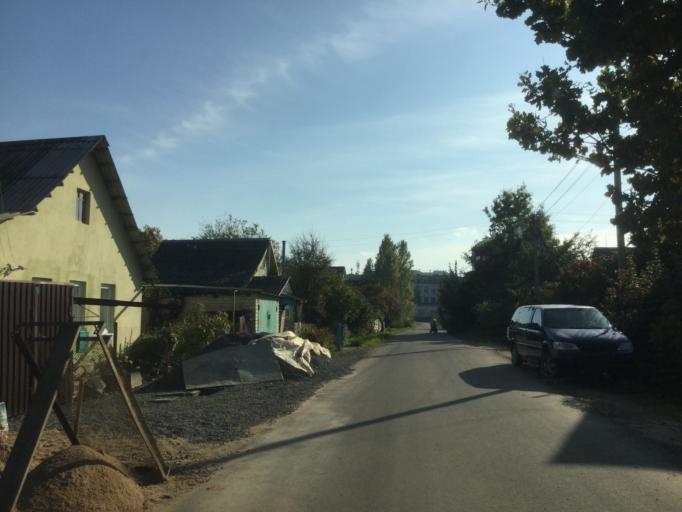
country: BY
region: Vitebsk
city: Vitebsk
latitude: 55.1901
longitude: 30.2371
